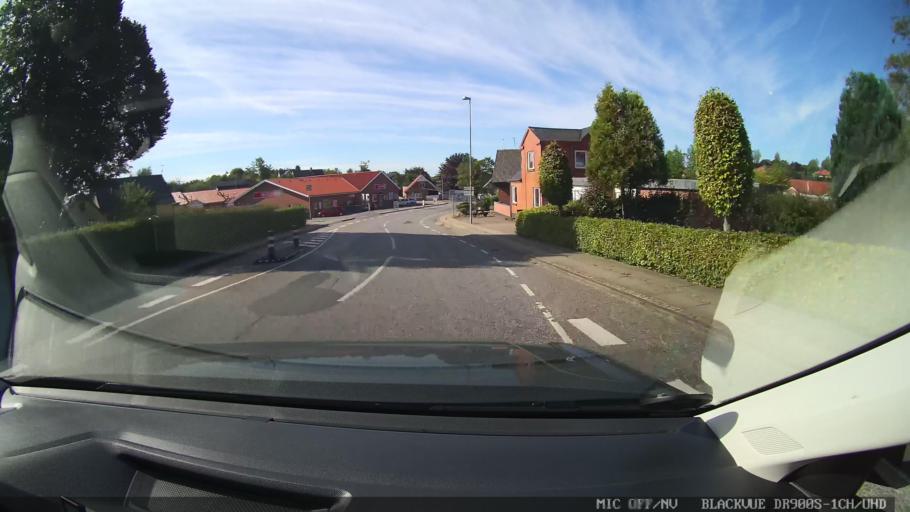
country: DK
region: North Denmark
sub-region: Mariagerfjord Kommune
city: Hobro
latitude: 56.6740
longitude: 9.8554
